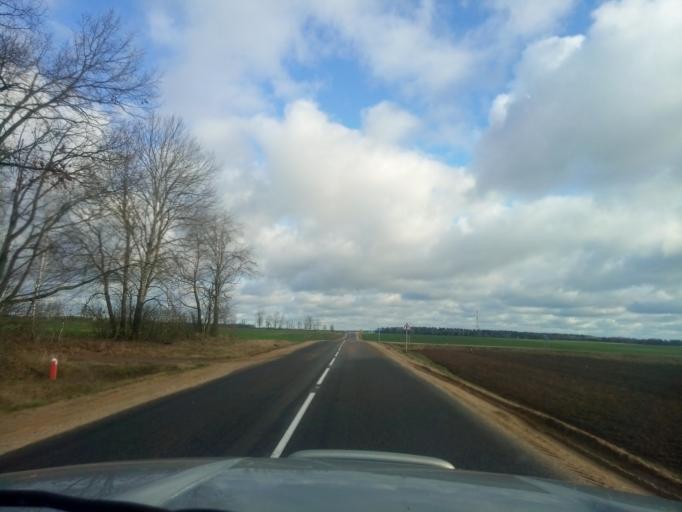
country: BY
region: Minsk
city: Kapyl'
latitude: 53.1415
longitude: 27.0198
